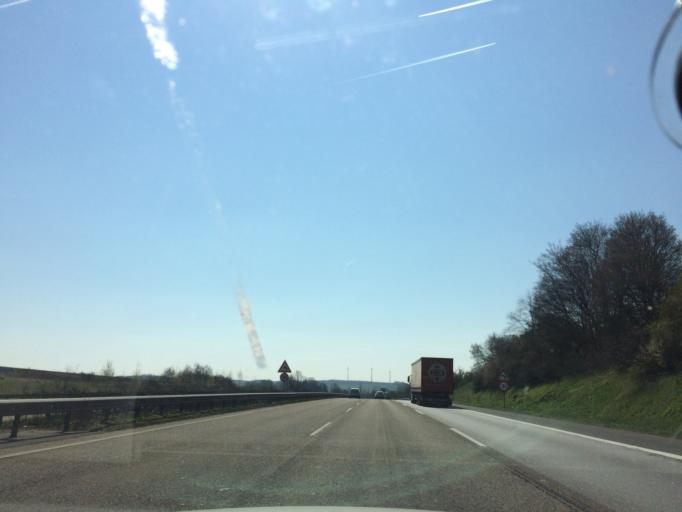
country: DE
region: Rheinland-Pfalz
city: Eppenrod
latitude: 50.4223
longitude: 7.9276
